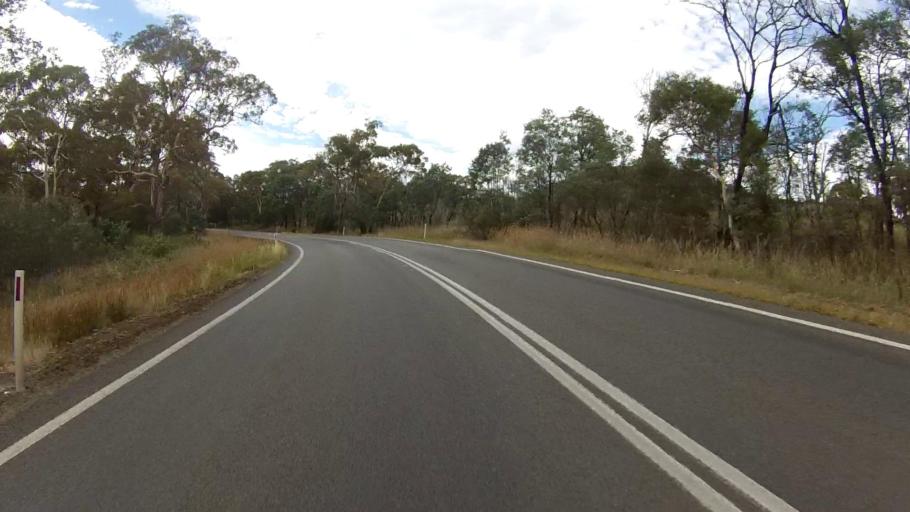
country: AU
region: Tasmania
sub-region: Sorell
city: Sorell
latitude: -42.7022
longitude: 147.4898
